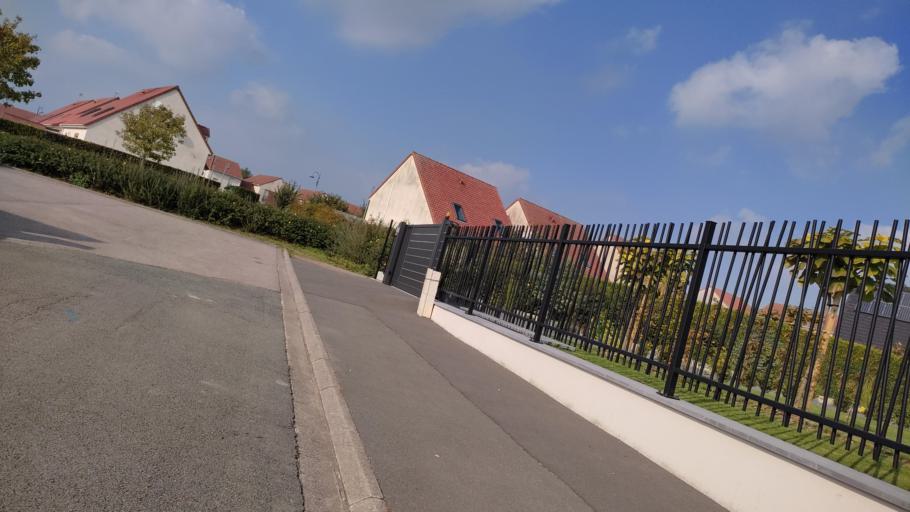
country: FR
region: Nord-Pas-de-Calais
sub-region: Departement du Pas-de-Calais
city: Dainville
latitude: 50.2844
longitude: 2.7208
